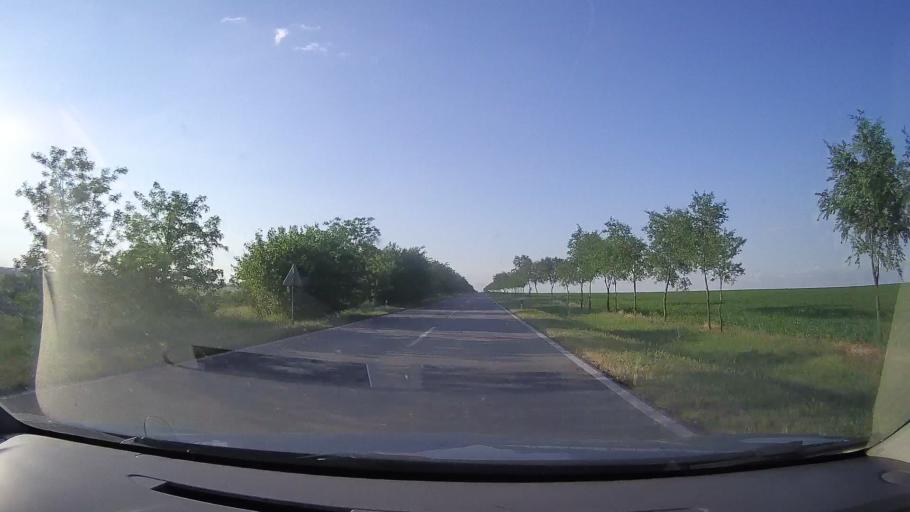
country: RO
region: Timis
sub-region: Comuna Moravita
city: Moravita
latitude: 45.2007
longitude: 21.2999
